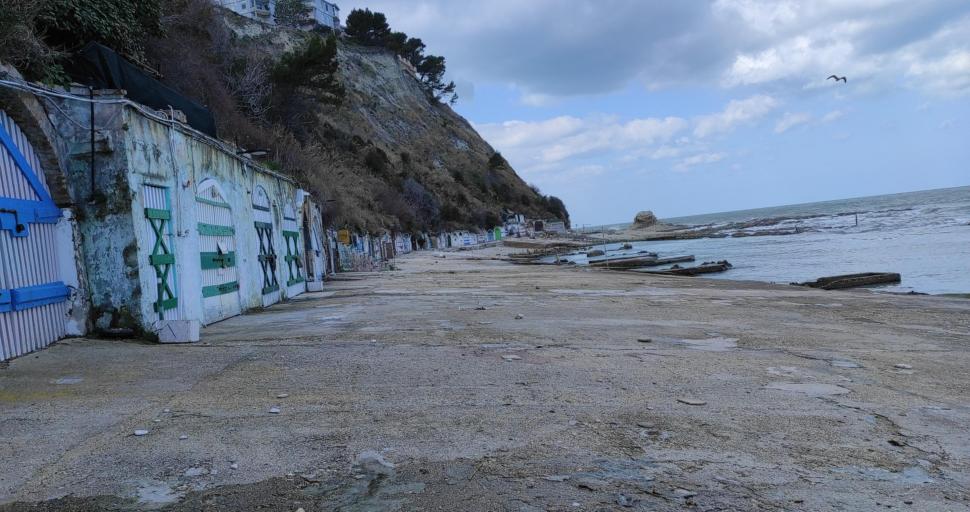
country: IT
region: The Marches
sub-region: Provincia di Ancona
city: Pietra la Croce
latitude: 43.6177
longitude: 13.5328
